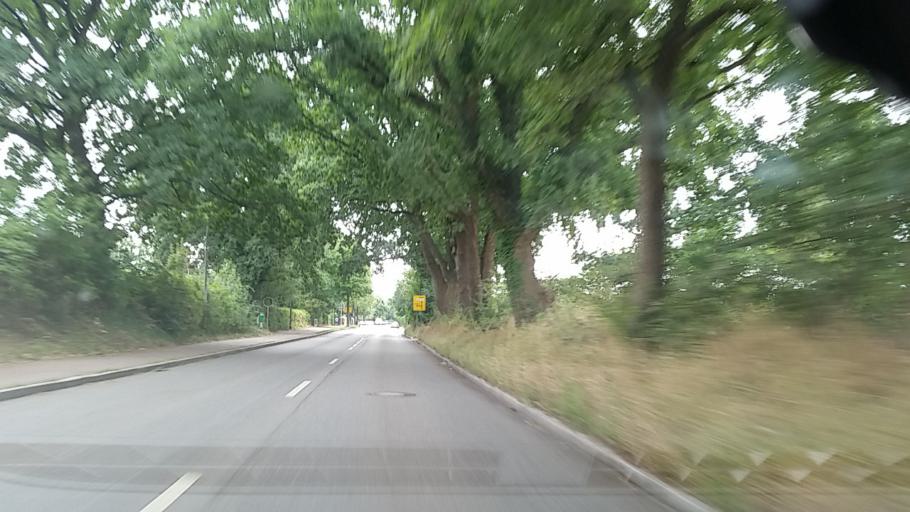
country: DE
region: Schleswig-Holstein
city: Reinbek
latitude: 53.5257
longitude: 10.2583
